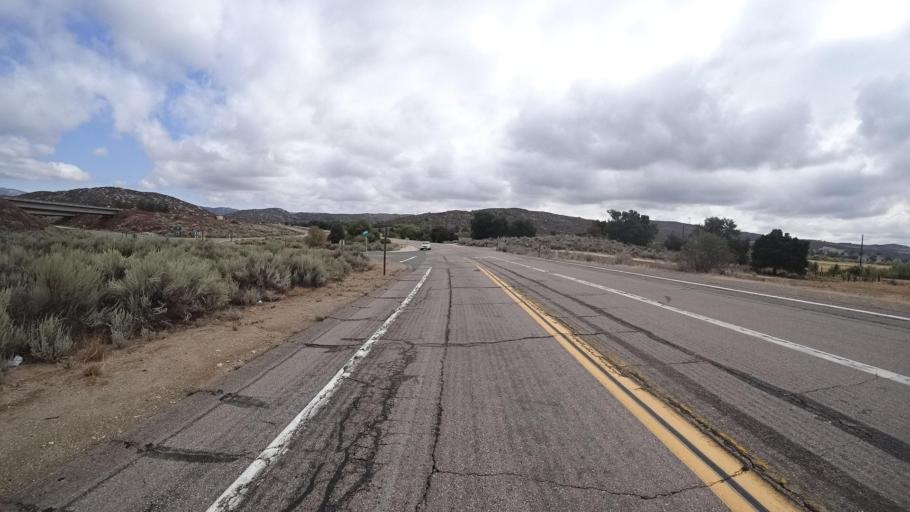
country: US
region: California
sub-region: San Diego County
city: Campo
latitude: 32.7174
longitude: -116.4722
